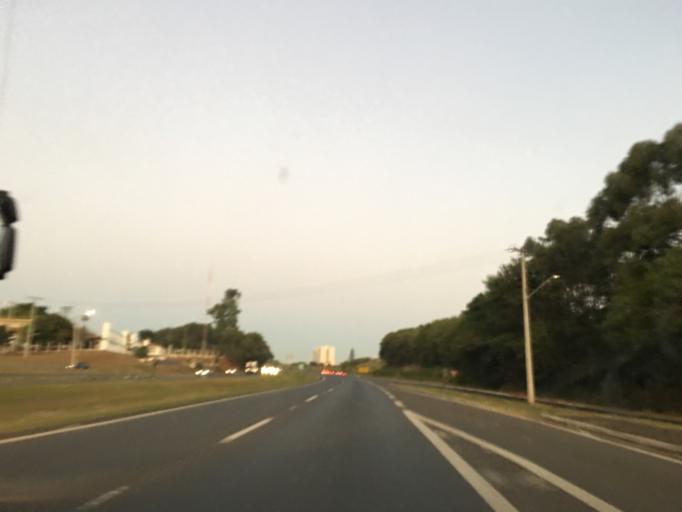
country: BR
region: Sao Paulo
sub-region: Piracicaba
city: Piracicaba
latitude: -22.7182
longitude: -47.6229
